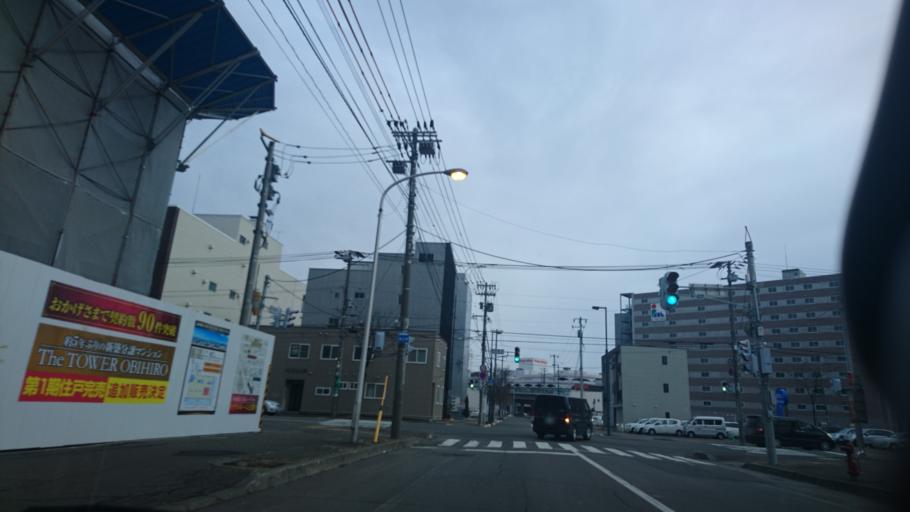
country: JP
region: Hokkaido
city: Obihiro
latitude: 42.9215
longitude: 143.1991
